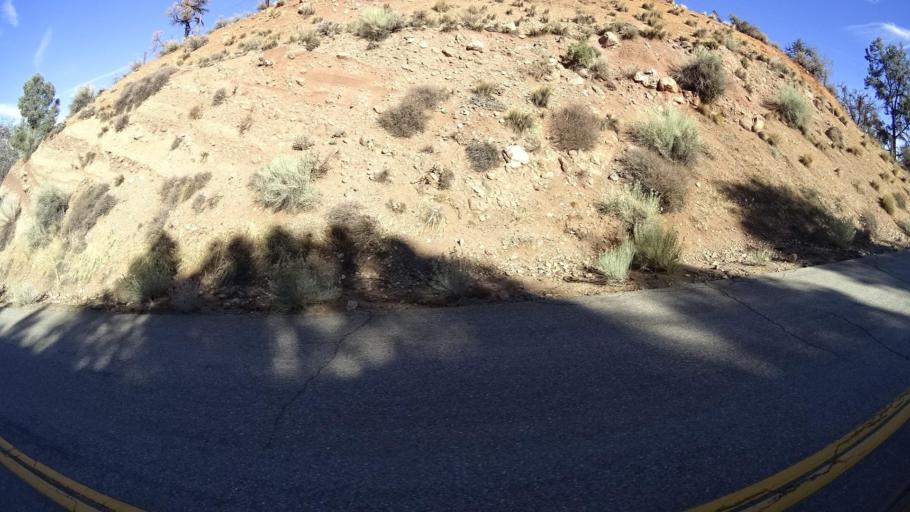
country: US
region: California
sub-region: Kern County
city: Maricopa
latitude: 34.8794
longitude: -119.3491
